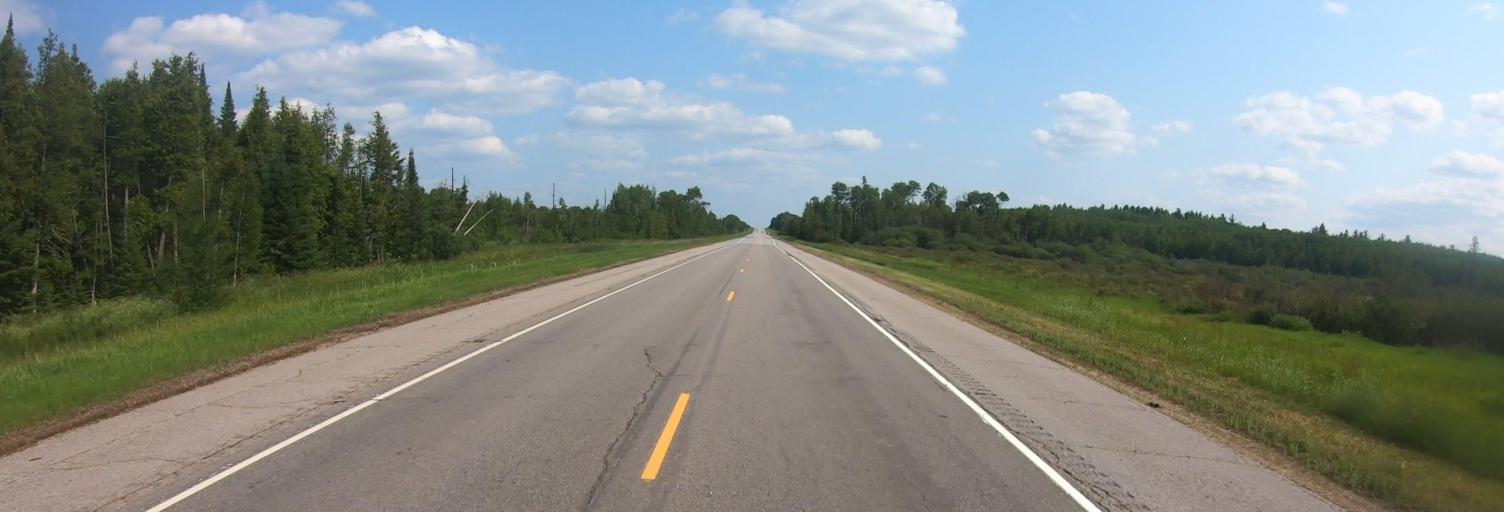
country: US
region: Minnesota
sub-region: Saint Louis County
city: Mountain Iron
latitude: 47.9237
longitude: -92.8219
